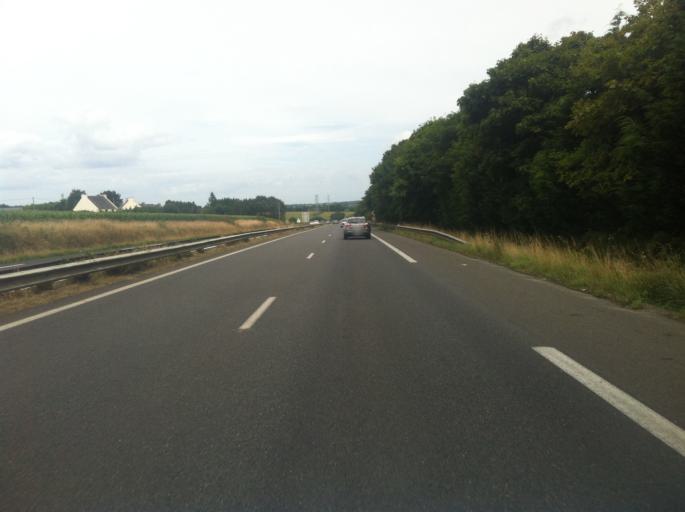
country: FR
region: Brittany
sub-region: Departement du Finistere
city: Morlaix
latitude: 48.5813
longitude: -3.8518
